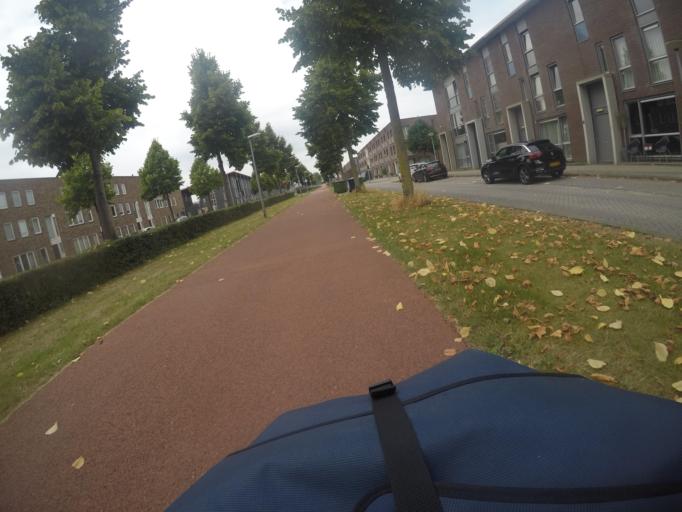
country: NL
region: Flevoland
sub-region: Gemeente Almere
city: Almere Stad
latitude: 52.3872
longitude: 5.1811
